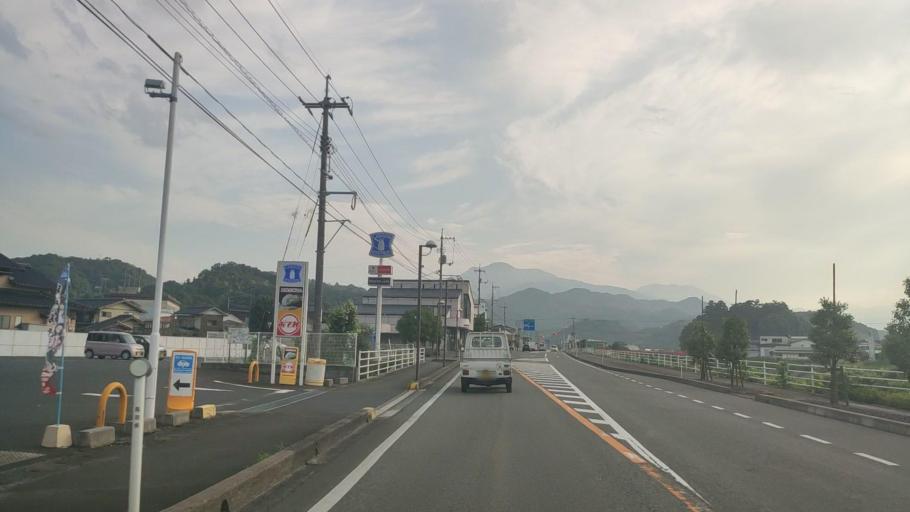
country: JP
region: Tottori
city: Kurayoshi
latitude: 35.3672
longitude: 133.7614
